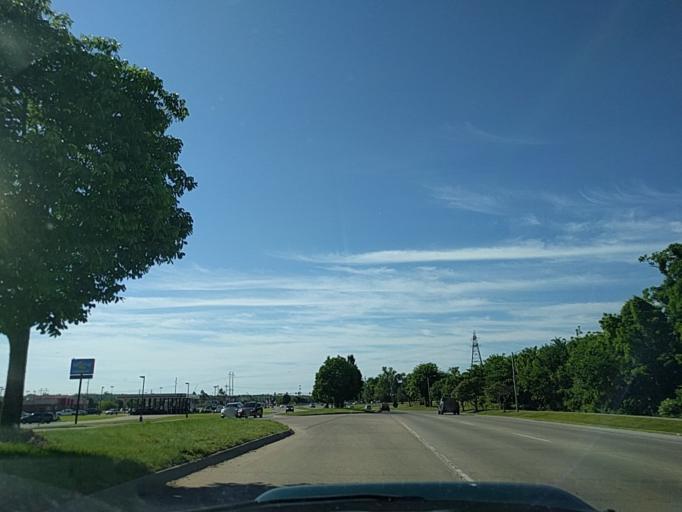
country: US
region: Oklahoma
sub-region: Tulsa County
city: Jenks
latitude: 36.0279
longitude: -95.9518
